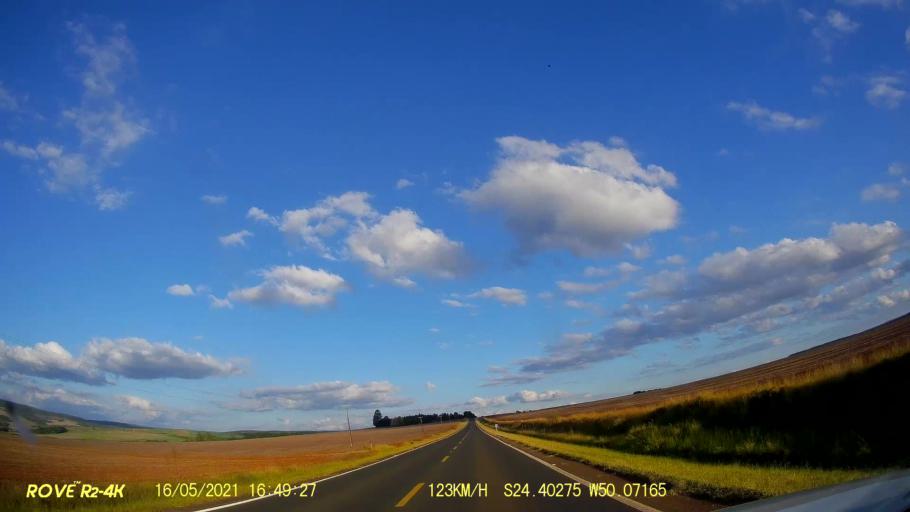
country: BR
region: Parana
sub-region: Pirai Do Sul
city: Pirai do Sul
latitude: -24.4029
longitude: -50.0715
